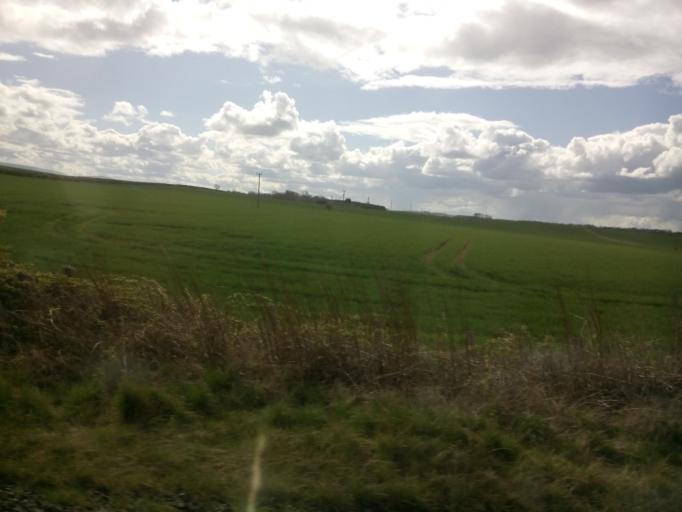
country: GB
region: England
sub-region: Northumberland
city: Ancroft
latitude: 55.7078
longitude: -1.9300
